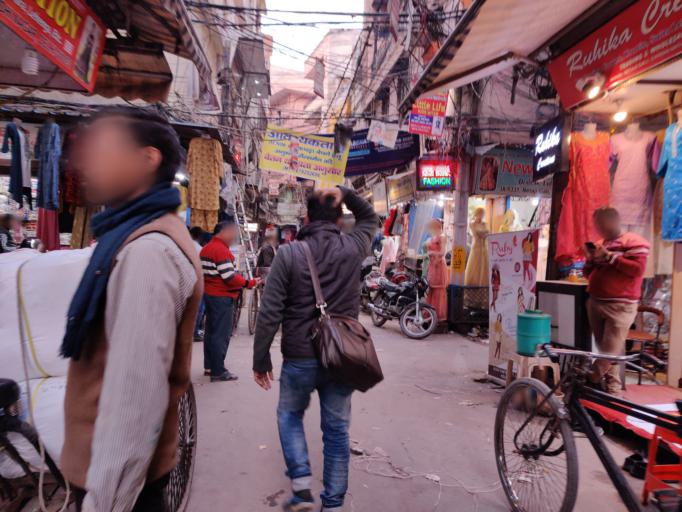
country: IN
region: NCT
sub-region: North Delhi
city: Delhi
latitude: 28.6613
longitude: 77.2654
